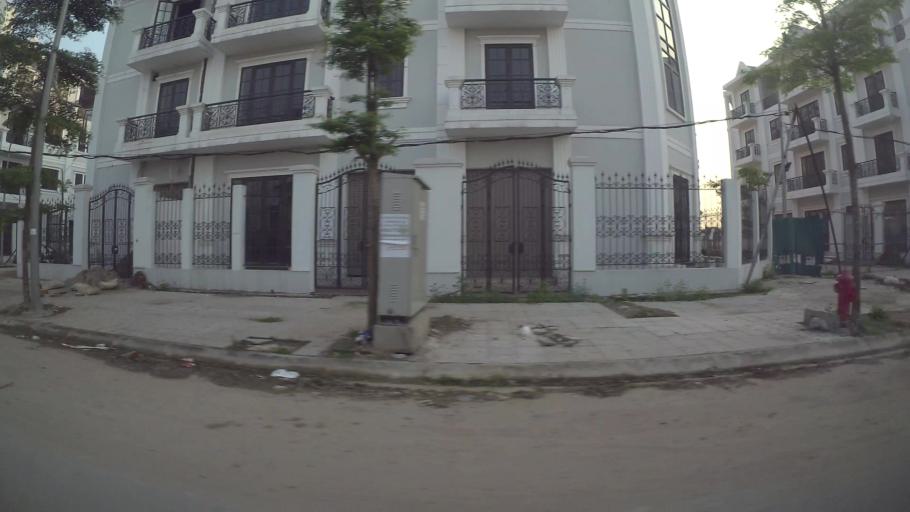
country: VN
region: Ha Noi
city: Thanh Xuan
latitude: 20.9757
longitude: 105.8180
